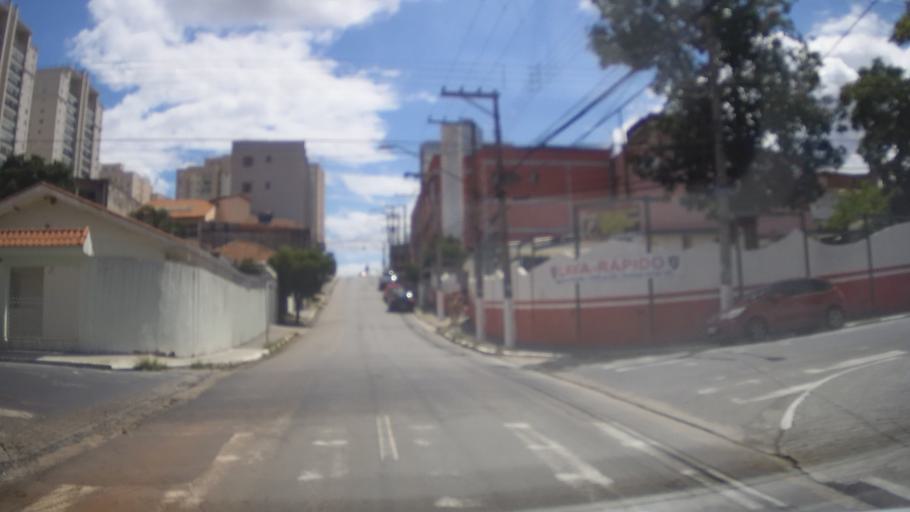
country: BR
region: Sao Paulo
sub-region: Guarulhos
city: Guarulhos
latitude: -23.4588
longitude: -46.5357
